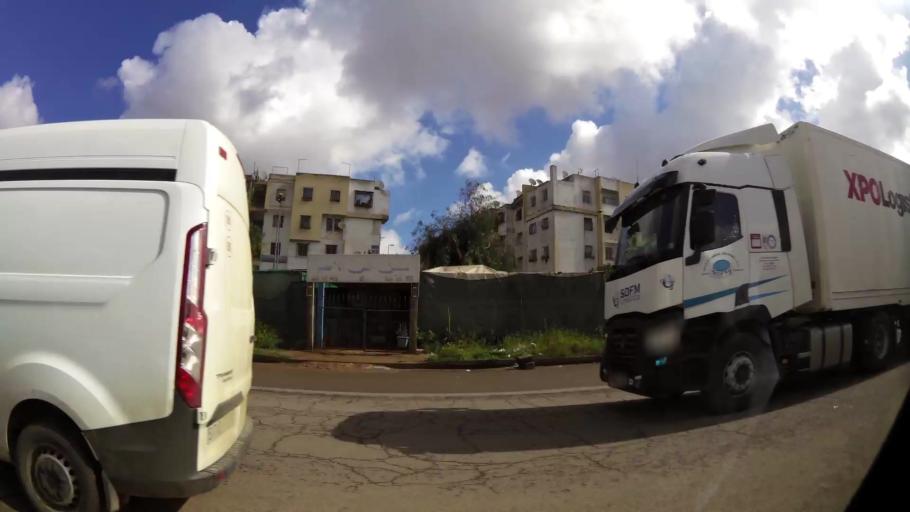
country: MA
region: Grand Casablanca
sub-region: Mediouna
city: Tit Mellil
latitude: 33.5691
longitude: -7.5170
